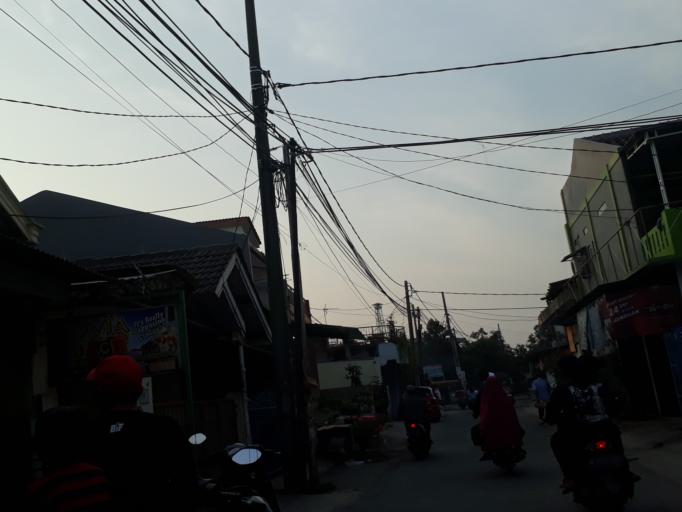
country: ID
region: West Java
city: Bekasi
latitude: -6.2445
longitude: 107.0527
